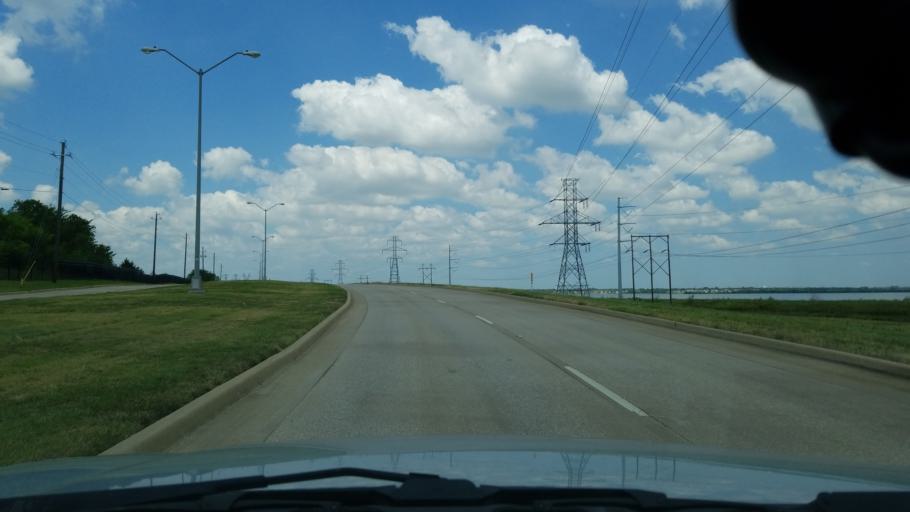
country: US
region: Texas
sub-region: Dallas County
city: Cockrell Hill
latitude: 32.7206
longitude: -96.9421
